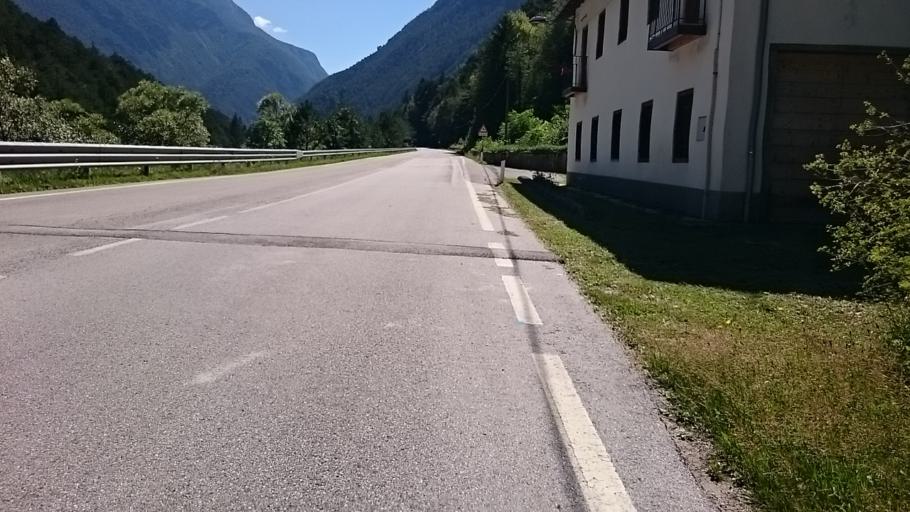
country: IT
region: Veneto
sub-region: Provincia di Belluno
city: Perarolo di Cadore
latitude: 46.3925
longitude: 12.3557
